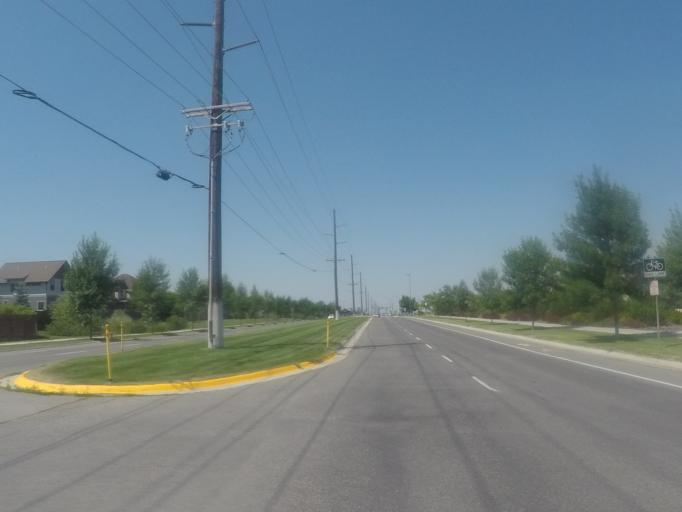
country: US
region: Montana
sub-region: Gallatin County
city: Bozeman
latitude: 45.6930
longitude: -111.0772
